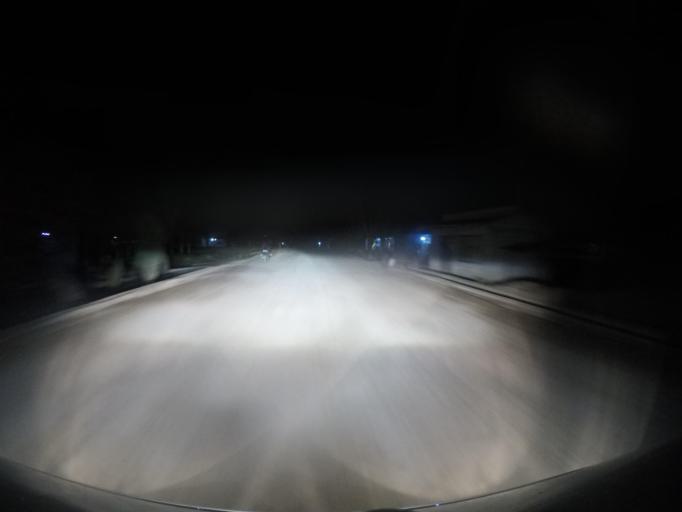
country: TL
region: Viqueque
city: Viqueque
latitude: -8.8044
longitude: 126.5466
